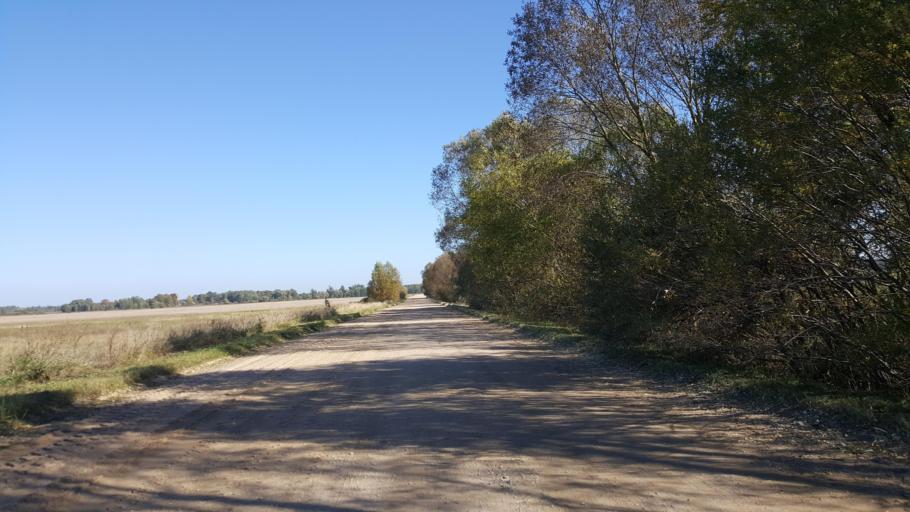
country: BY
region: Brest
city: Kamyanyets
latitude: 52.4150
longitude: 23.8609
